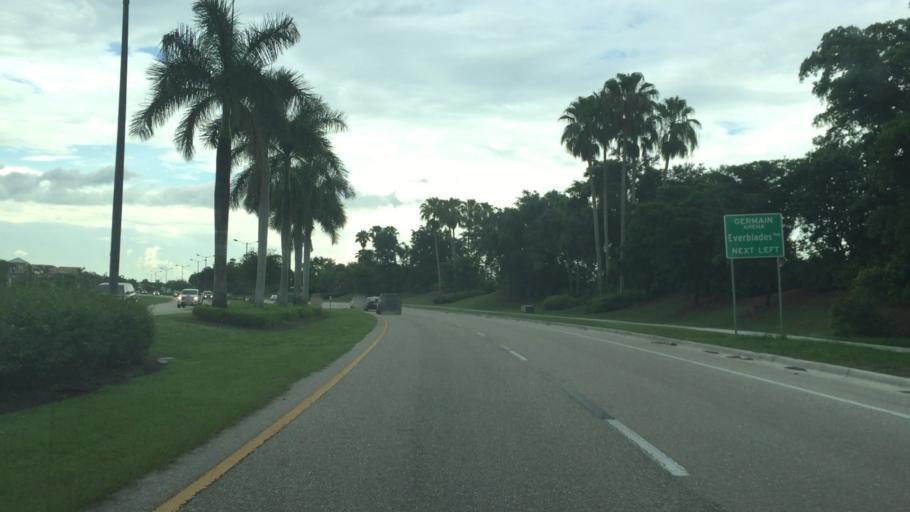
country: US
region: Florida
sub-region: Lee County
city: Estero
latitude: 26.4400
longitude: -81.7713
